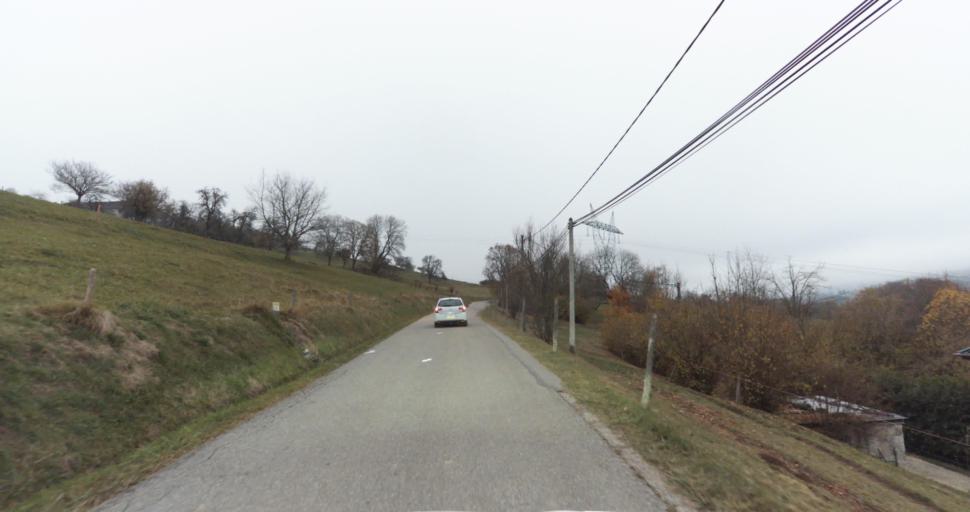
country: FR
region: Rhone-Alpes
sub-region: Departement de la Haute-Savoie
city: Saint-Jorioz
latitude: 45.7876
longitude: 6.1476
